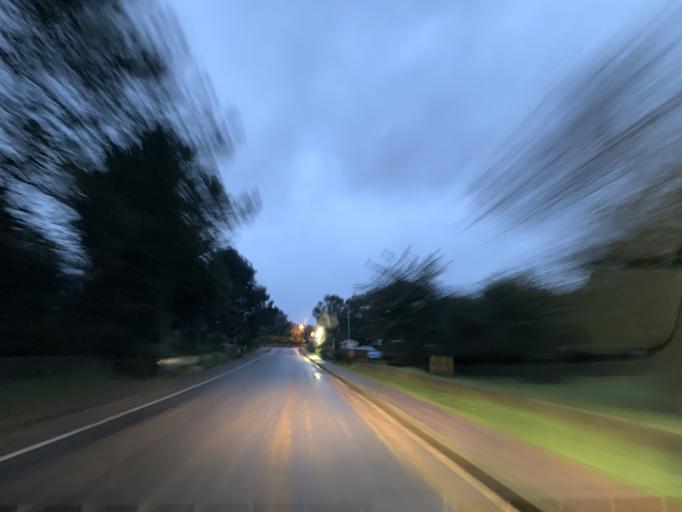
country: DE
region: Schleswig-Holstein
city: Nebel
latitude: 54.6411
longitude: 8.3575
